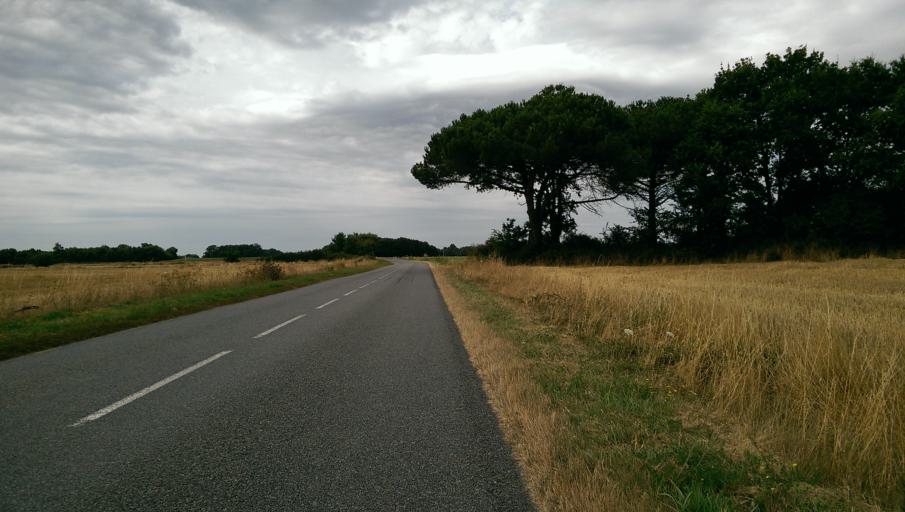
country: FR
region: Pays de la Loire
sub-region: Departement de la Loire-Atlantique
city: La Planche
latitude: 46.9985
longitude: -1.4296
